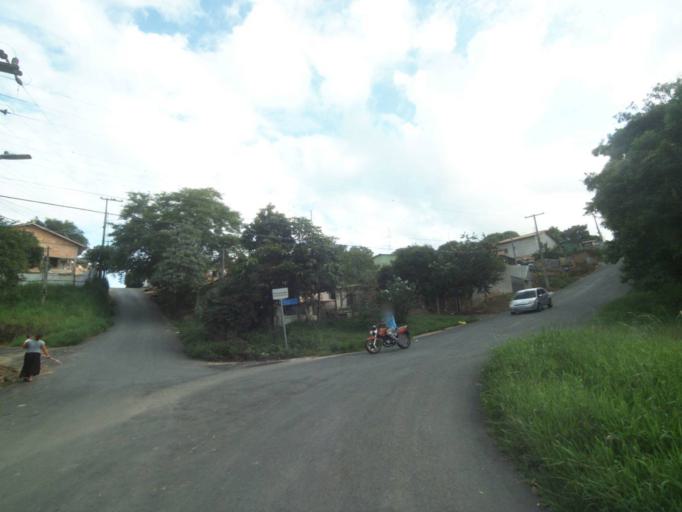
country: BR
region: Parana
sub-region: Telemaco Borba
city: Telemaco Borba
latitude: -24.3253
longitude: -50.6078
